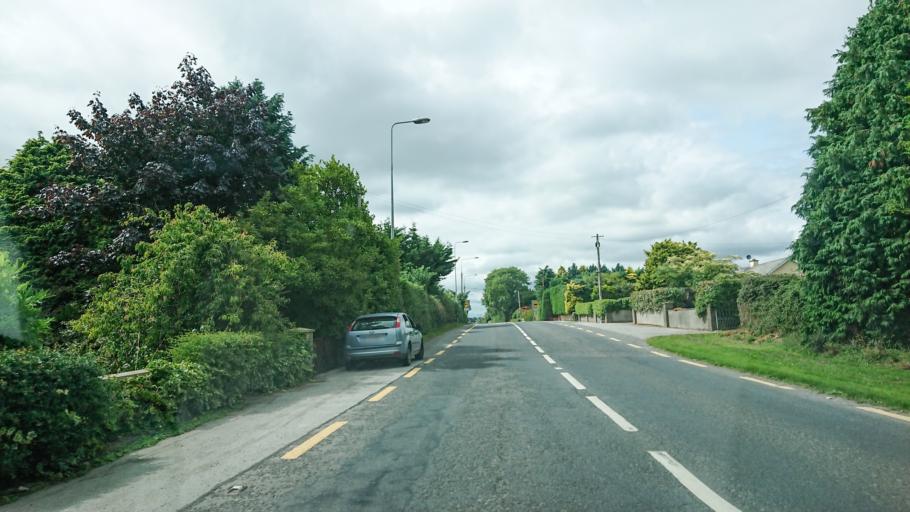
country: IE
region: Munster
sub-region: Waterford
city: Dungarvan
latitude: 52.1083
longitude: -7.6640
